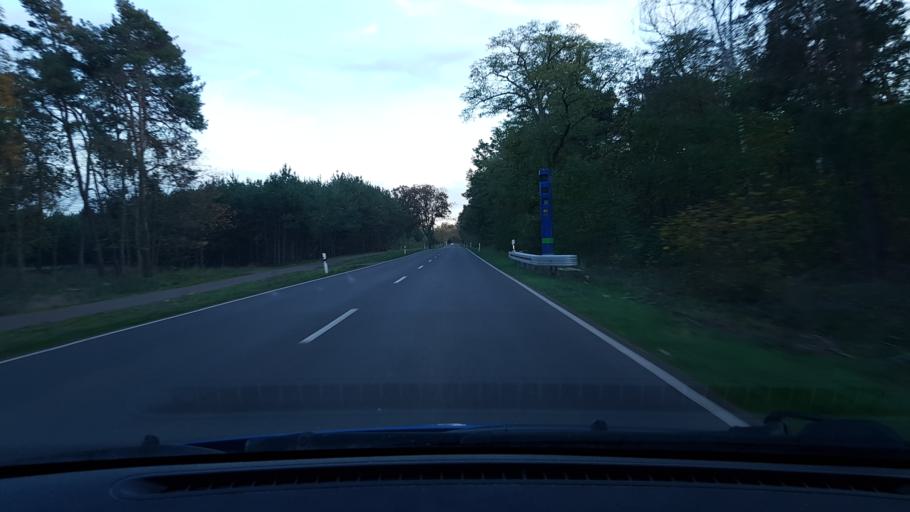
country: DE
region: Saxony-Anhalt
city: Wahlitz
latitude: 52.1003
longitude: 11.7847
